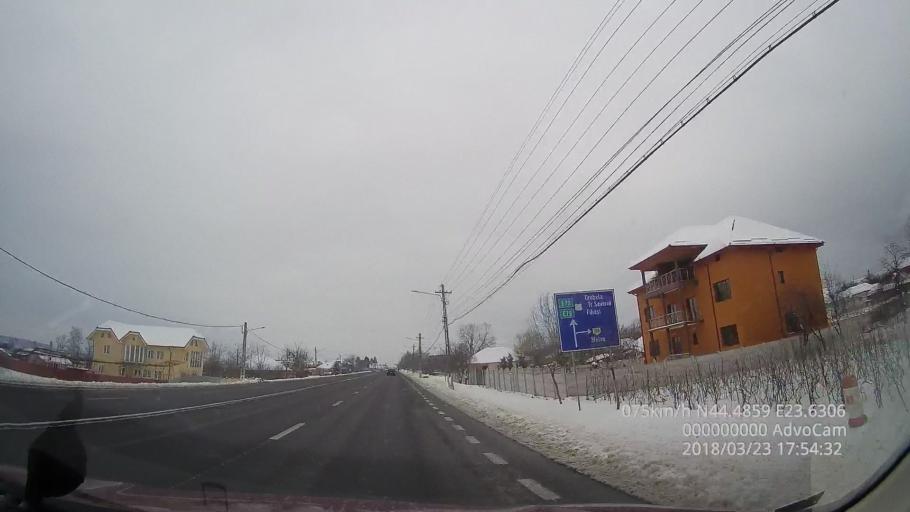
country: RO
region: Dolj
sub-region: Comuna Bradesti
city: Bradesti
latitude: 44.4861
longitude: 23.6304
